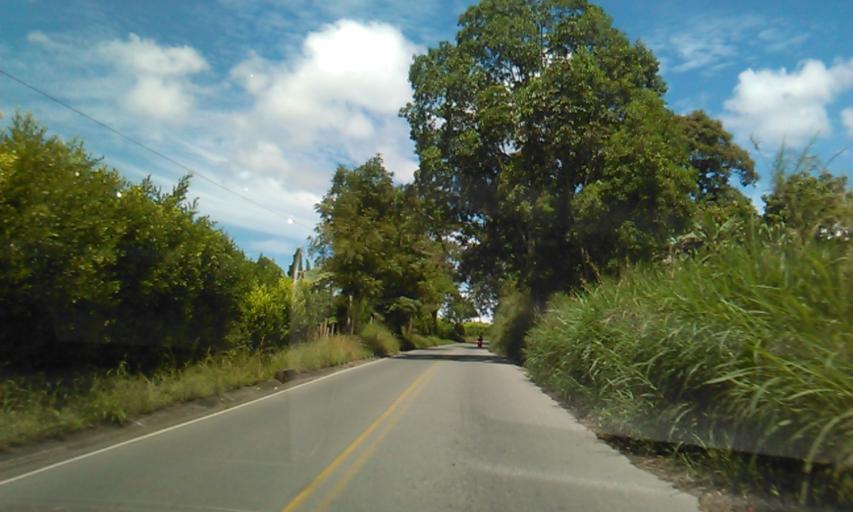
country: CO
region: Quindio
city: Cordoba
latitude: 4.4101
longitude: -75.7273
